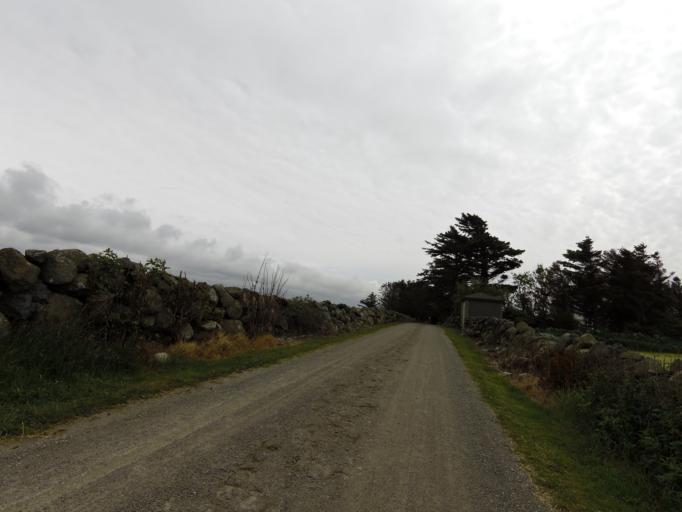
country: NO
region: Rogaland
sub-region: Ha
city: Naerbo
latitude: 58.6709
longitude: 5.5519
